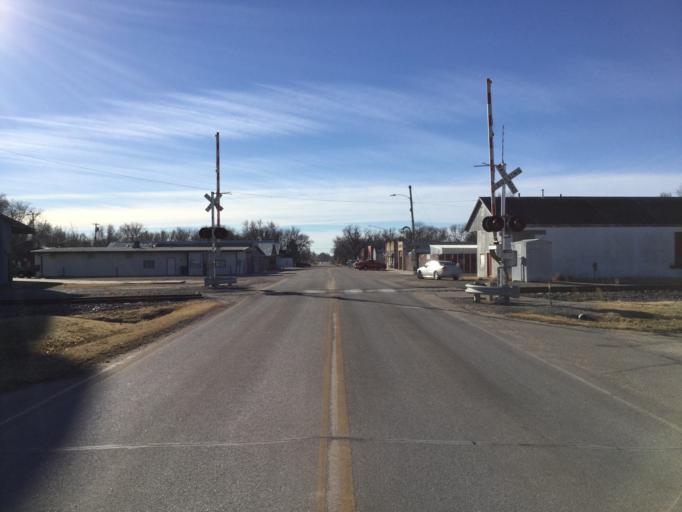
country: US
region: Kansas
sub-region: Butler County
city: Andover
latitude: 37.7894
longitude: -97.1080
